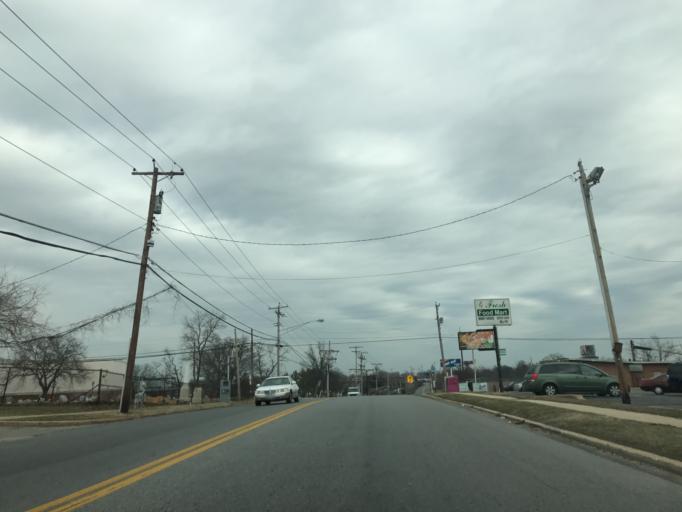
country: US
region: Maryland
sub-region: Baltimore County
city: Lansdowne
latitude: 39.2425
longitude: -76.6501
